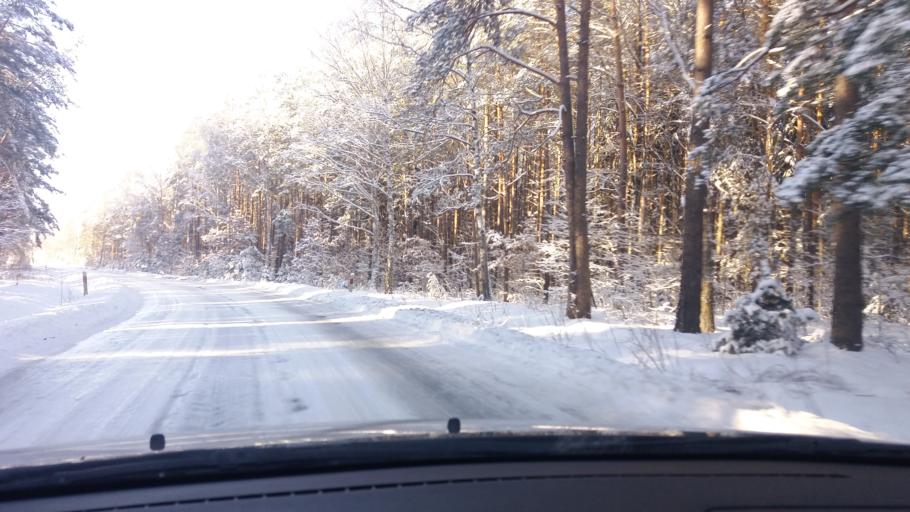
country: PL
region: Masovian Voivodeship
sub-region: Powiat mlawski
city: Dzierzgowo
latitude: 53.3332
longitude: 20.6414
